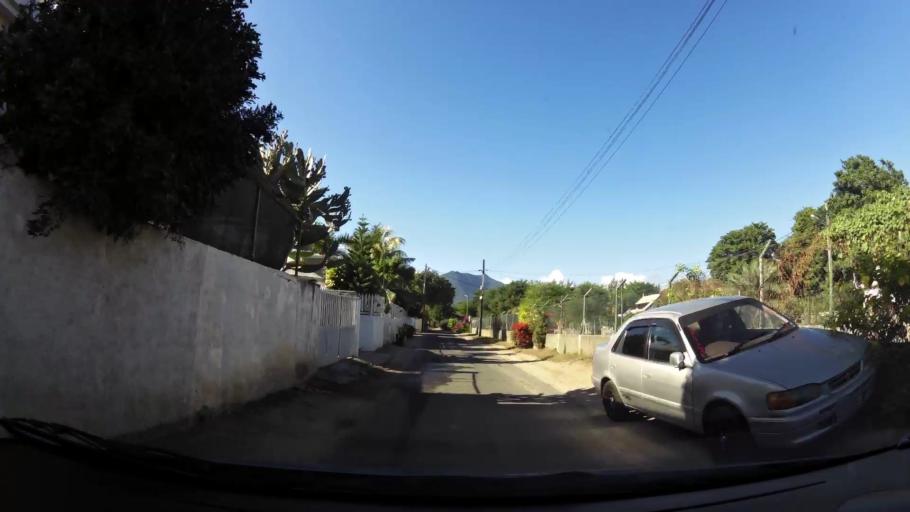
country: MU
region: Black River
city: Grande Riviere Noire
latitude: -20.3570
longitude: 57.3645
